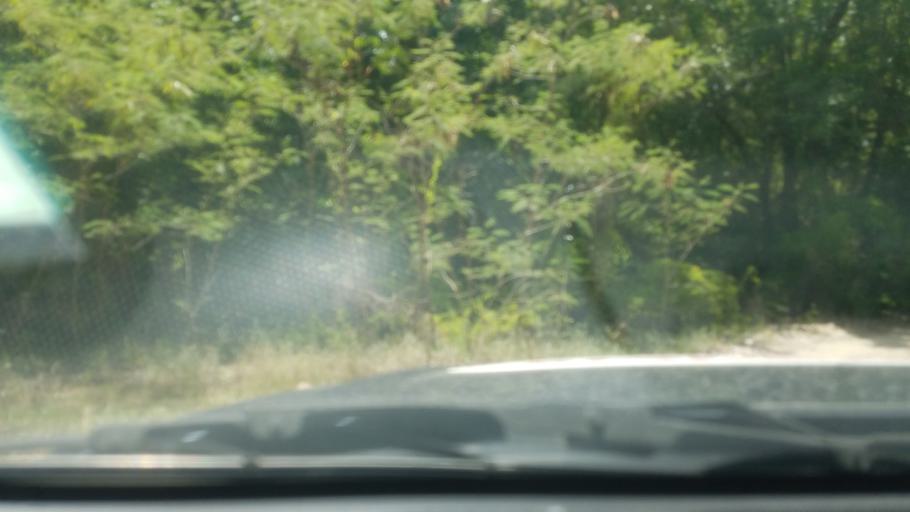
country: LC
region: Vieux-Fort
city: Vieux Fort
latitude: 13.7466
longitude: -60.9379
